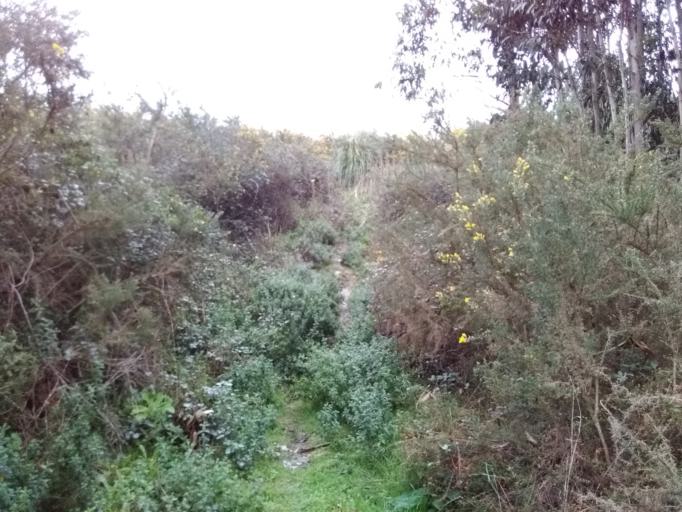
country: ES
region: Galicia
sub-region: Provincia da Coruna
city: A Coruna
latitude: 43.3296
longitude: -8.4384
